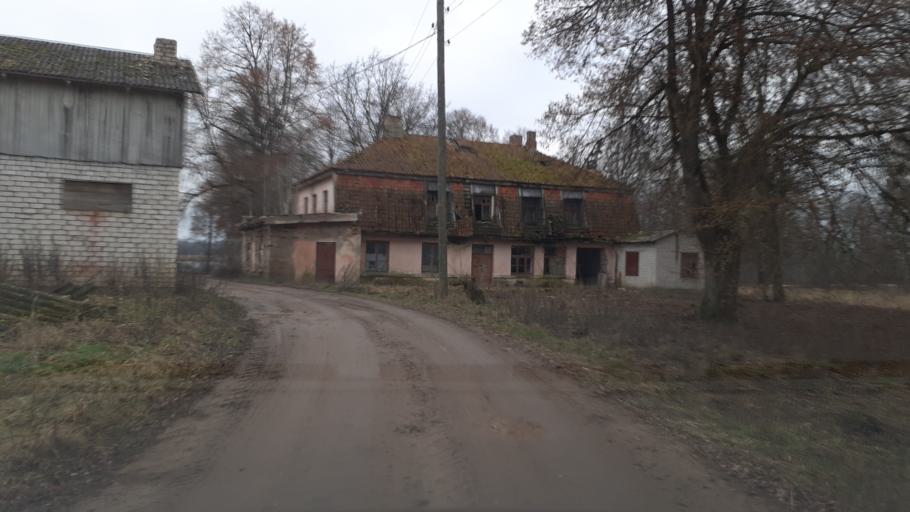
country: LV
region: Aizpute
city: Aizpute
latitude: 56.8027
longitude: 21.6667
